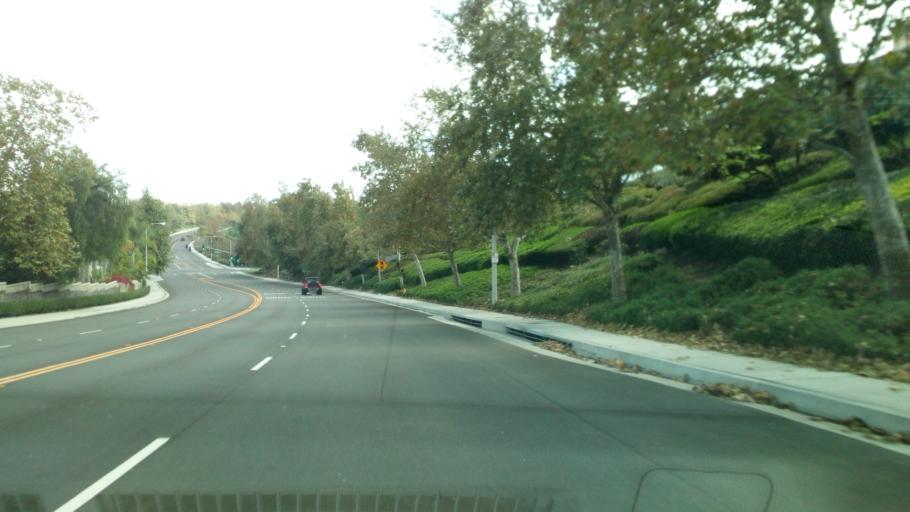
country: US
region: California
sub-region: Orange County
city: Aliso Viejo
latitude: 33.5641
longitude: -117.7365
